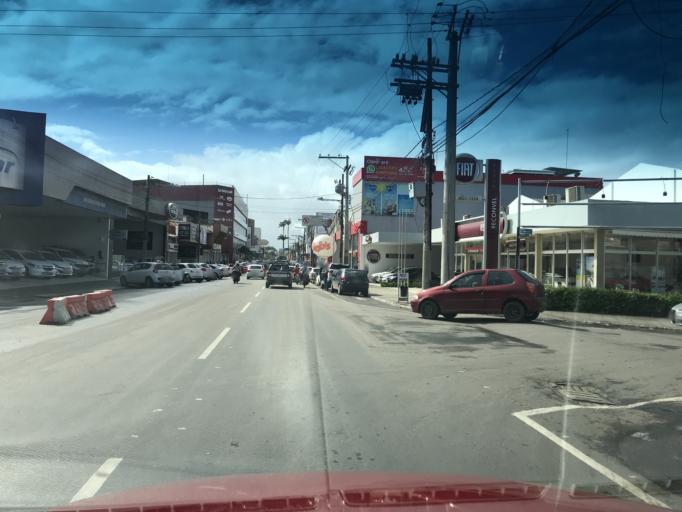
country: BR
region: Bahia
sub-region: Santo Antonio De Jesus
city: Santo Antonio de Jesus
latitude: -12.9663
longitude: -39.2697
